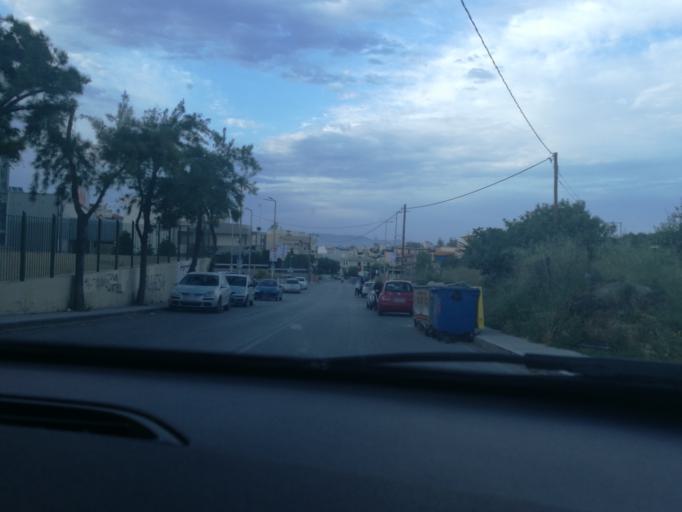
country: GR
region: Crete
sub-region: Nomos Irakleiou
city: Irakleion
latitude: 35.3179
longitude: 25.1484
